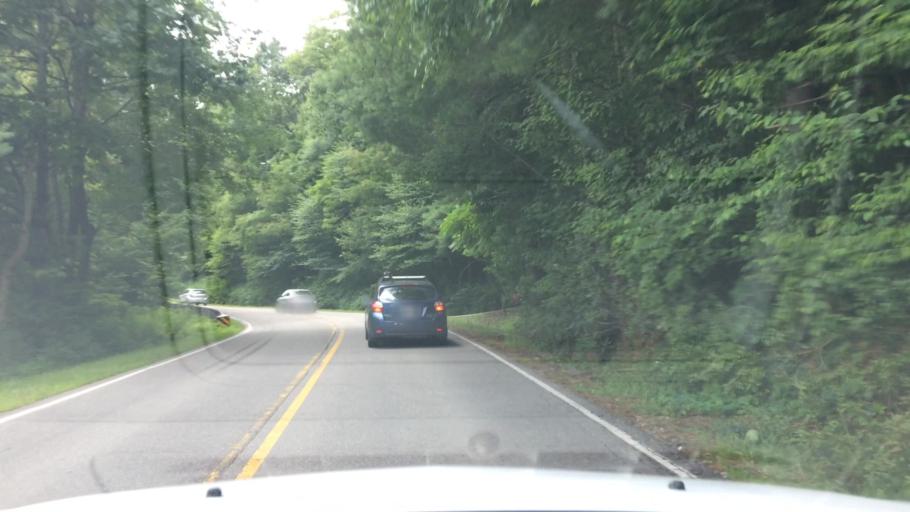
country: US
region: North Carolina
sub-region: Watauga County
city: Boone
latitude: 36.2087
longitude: -81.6309
